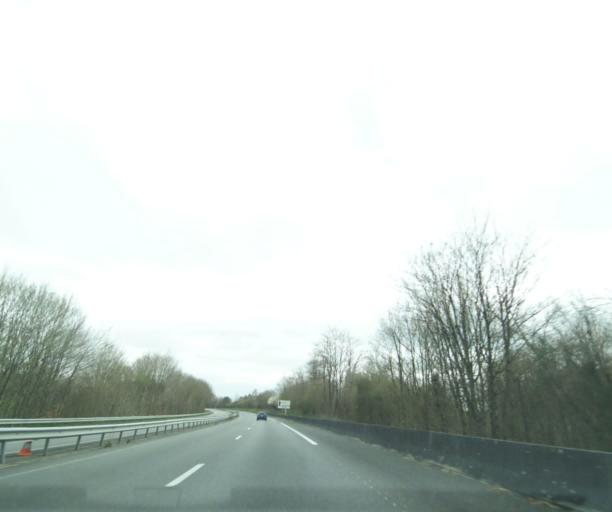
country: FR
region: Limousin
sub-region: Departement de la Haute-Vienne
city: Saint-Germain-les-Belles
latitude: 45.5976
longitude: 1.4492
